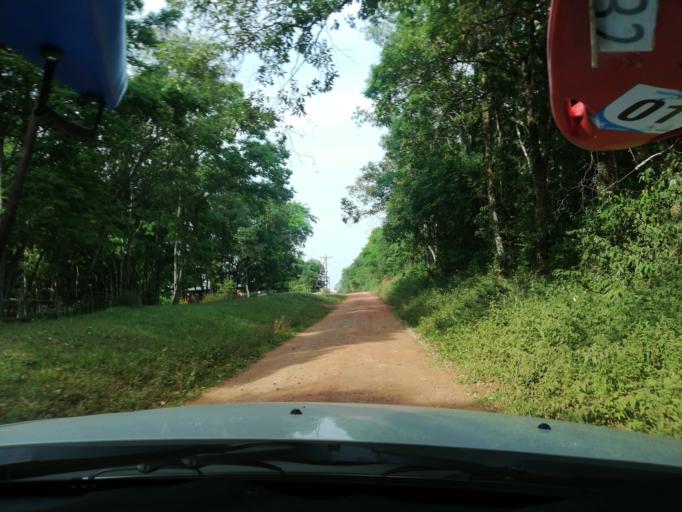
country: AR
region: Misiones
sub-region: Departamento de San Ignacio
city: San Ignacio
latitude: -27.2992
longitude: -55.5742
